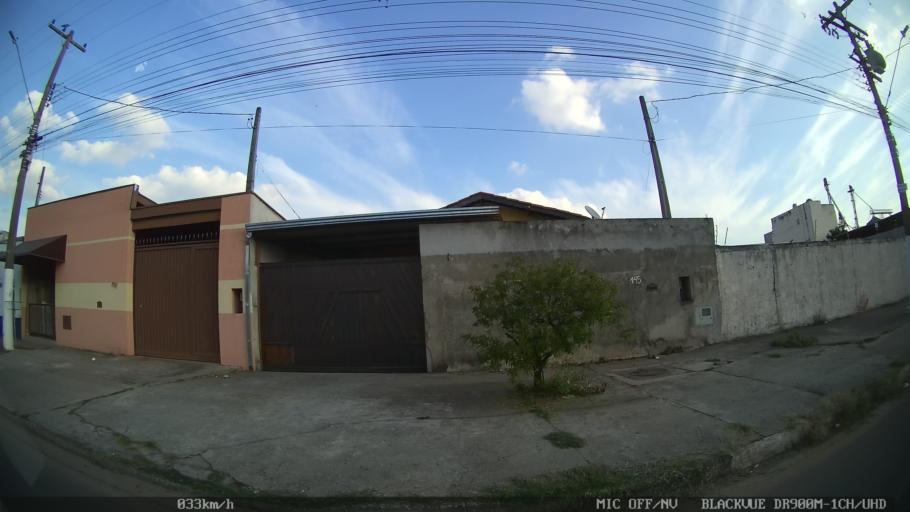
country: BR
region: Sao Paulo
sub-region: Hortolandia
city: Hortolandia
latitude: -22.8773
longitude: -47.1706
